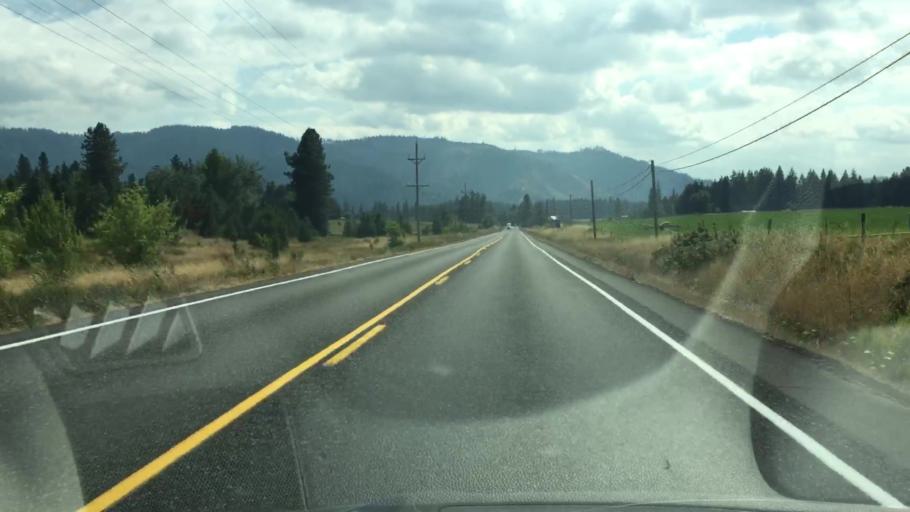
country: US
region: Washington
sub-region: Klickitat County
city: White Salmon
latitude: 45.8177
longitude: -121.4883
